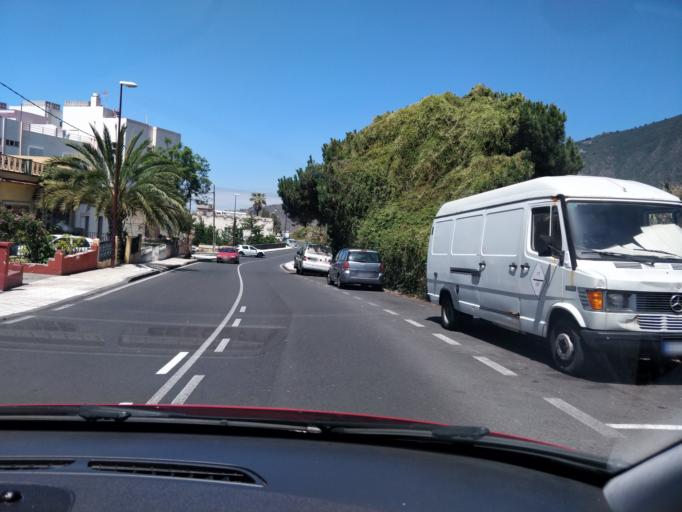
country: ES
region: Canary Islands
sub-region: Provincia de Santa Cruz de Tenerife
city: La Orotava
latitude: 28.3872
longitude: -16.5223
